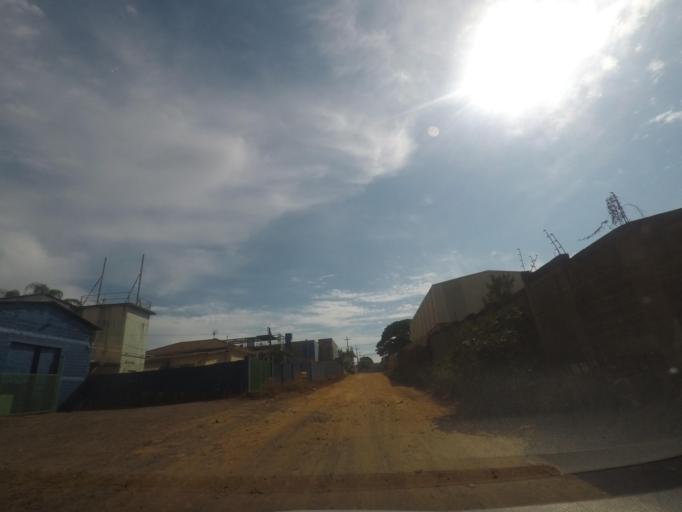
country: BR
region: Sao Paulo
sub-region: Sumare
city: Sumare
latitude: -22.7921
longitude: -47.2295
